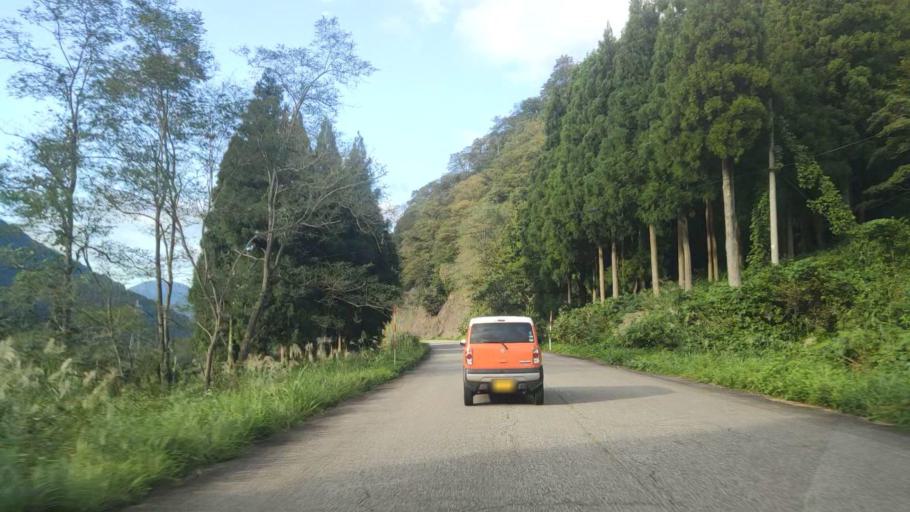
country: JP
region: Toyama
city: Yatsuomachi-higashikumisaka
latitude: 36.4501
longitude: 137.0845
